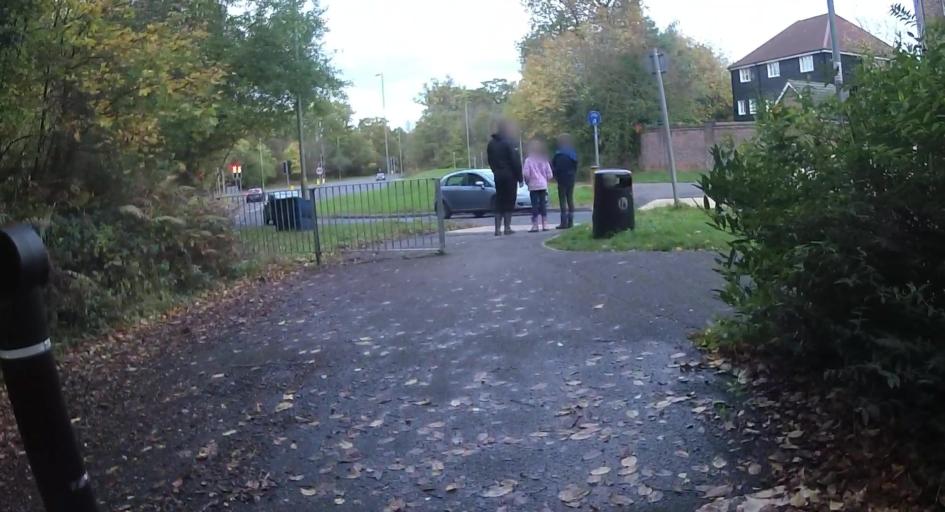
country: GB
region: England
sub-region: Hampshire
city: Old Basing
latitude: 51.2880
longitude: -1.0526
